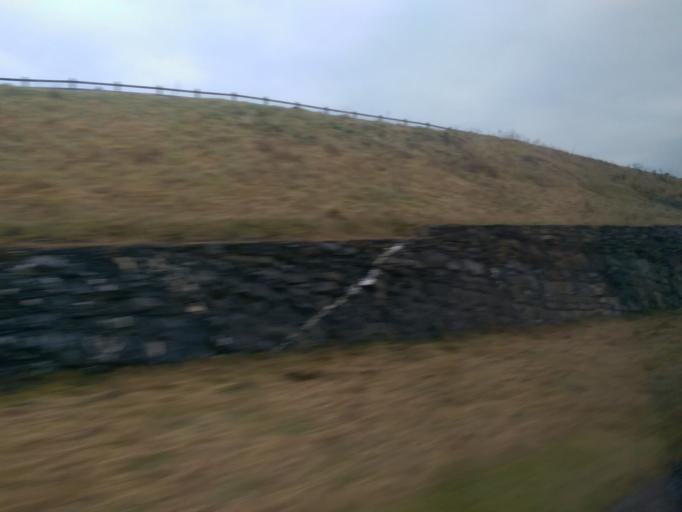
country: IE
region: Connaught
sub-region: County Galway
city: Loughrea
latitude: 53.2815
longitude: -8.4341
